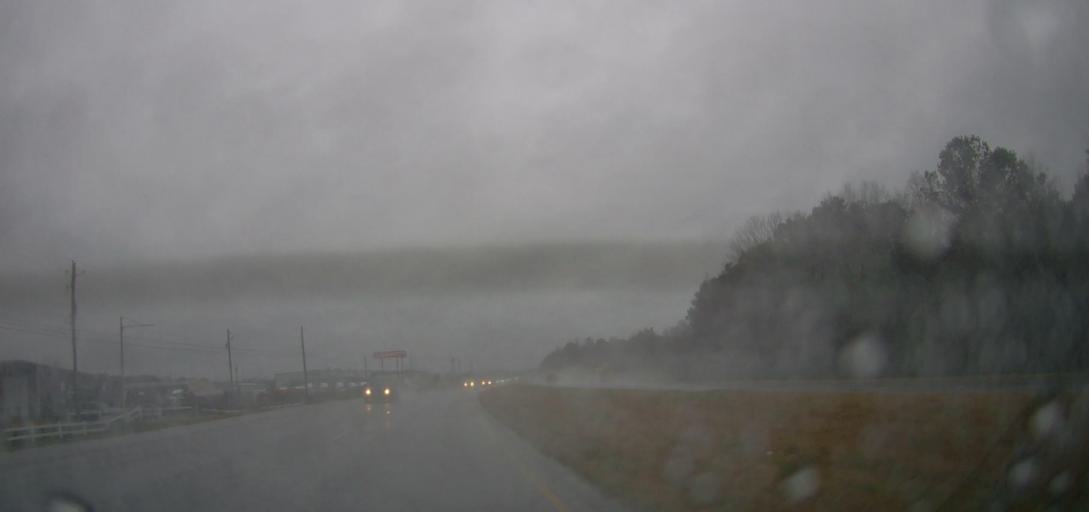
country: US
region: Alabama
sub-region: Montgomery County
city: Montgomery
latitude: 32.3827
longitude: -86.3797
